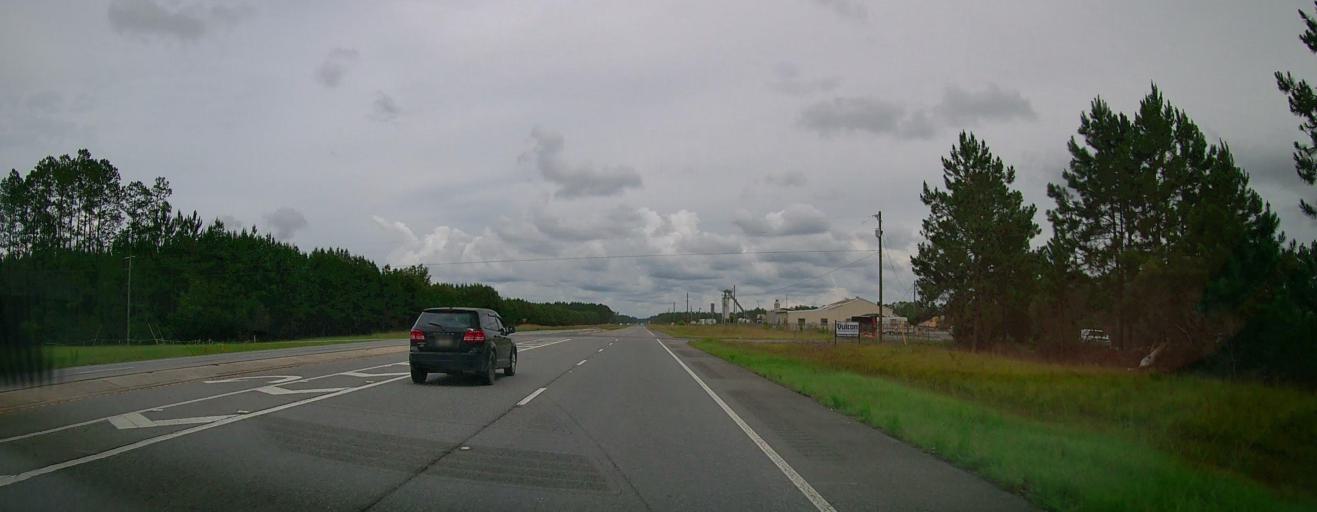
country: US
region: Georgia
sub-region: Appling County
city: Baxley
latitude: 31.7380
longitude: -82.2328
